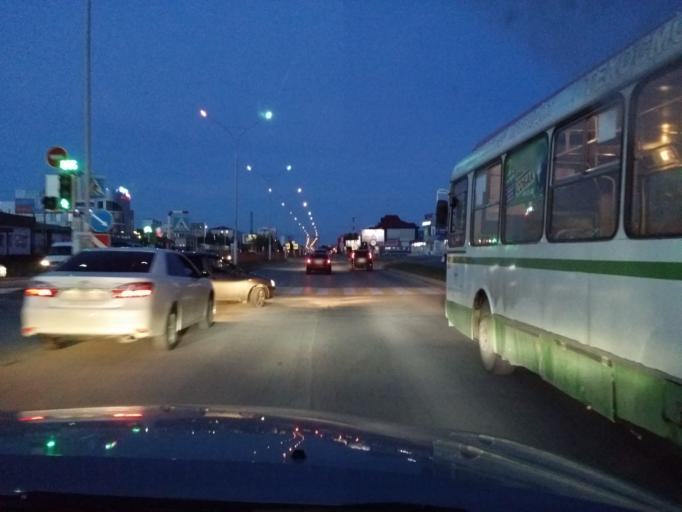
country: RU
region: Khanty-Mansiyskiy Avtonomnyy Okrug
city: Nizhnevartovsk
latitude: 60.9389
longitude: 76.5408
